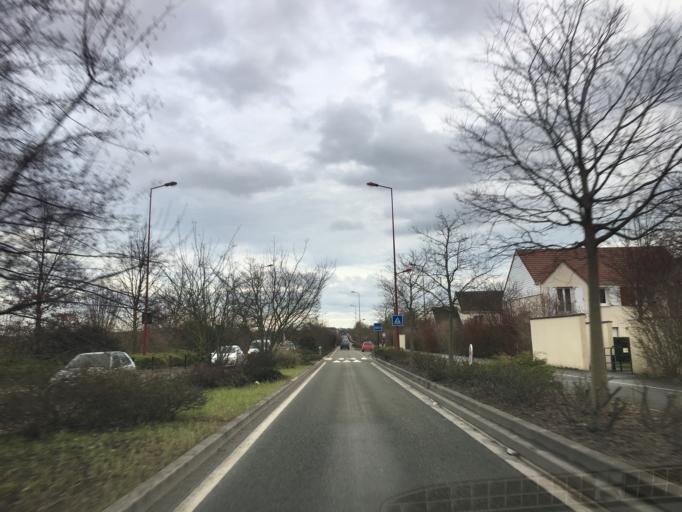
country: FR
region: Ile-de-France
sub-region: Departement du Val-d'Oise
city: Gonesse
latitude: 48.9998
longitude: 2.4327
